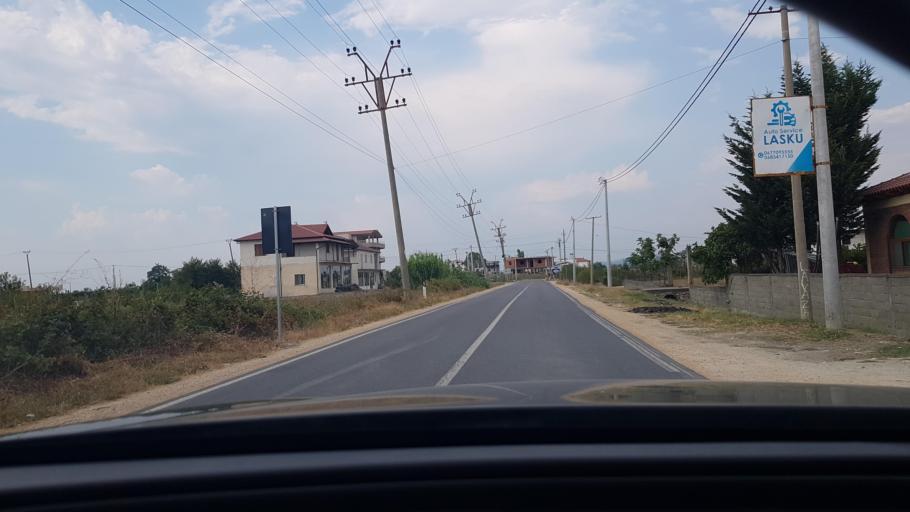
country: AL
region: Durres
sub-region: Rrethi i Durresit
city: Katundi i Ri
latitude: 41.4108
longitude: 19.5469
